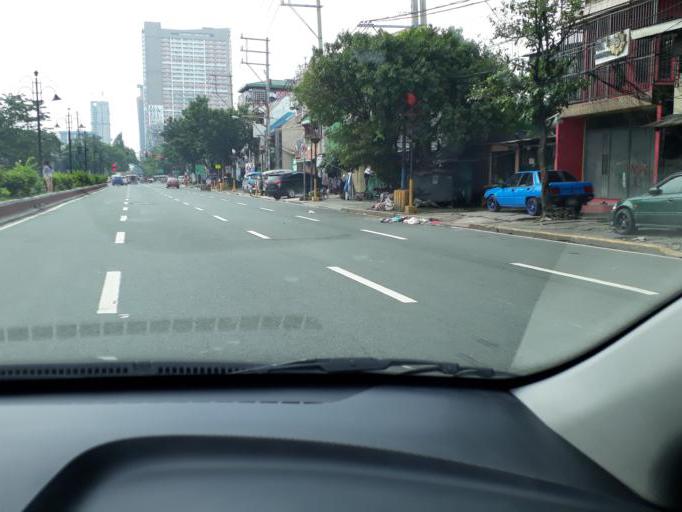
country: PH
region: Metro Manila
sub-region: City of Manila
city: Manila
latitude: 14.6063
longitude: 120.9960
